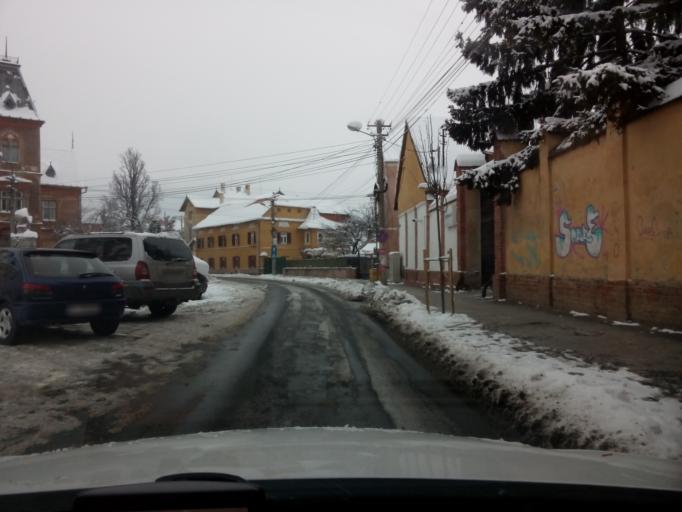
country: RO
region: Sibiu
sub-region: Municipiul Sibiu
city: Sibiu
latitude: 45.7923
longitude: 24.1430
